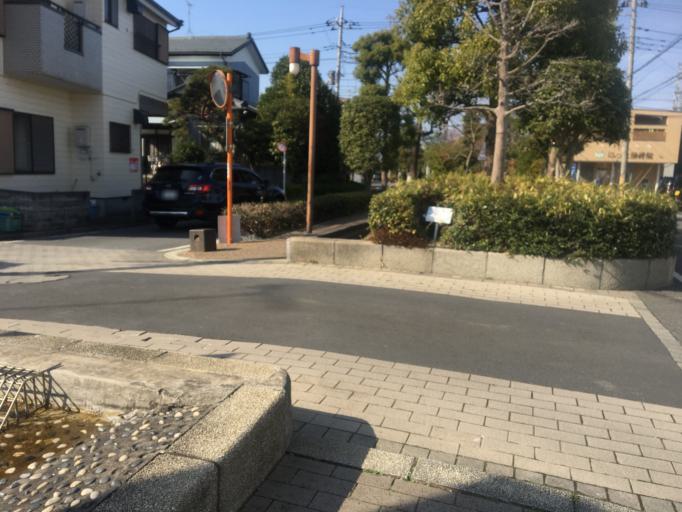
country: JP
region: Saitama
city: Shiki
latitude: 35.8396
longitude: 139.5881
